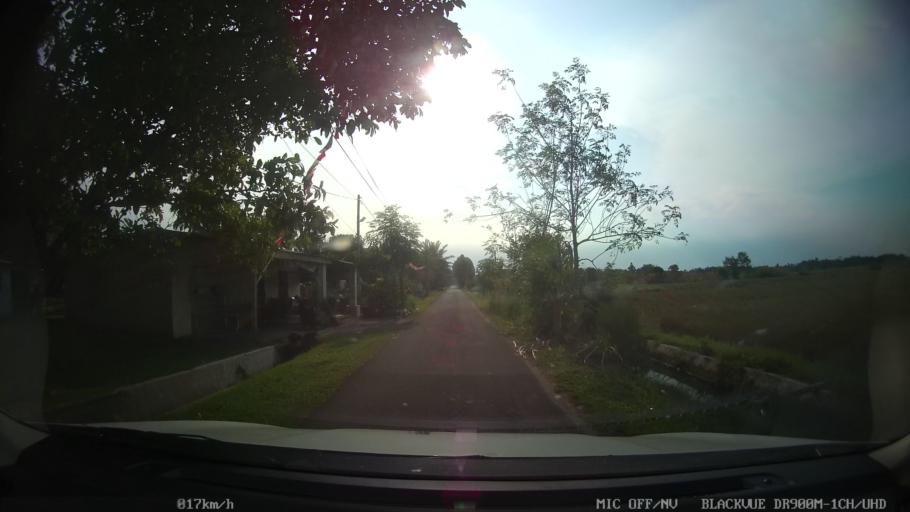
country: ID
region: North Sumatra
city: Binjai
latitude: 3.6210
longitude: 98.5282
